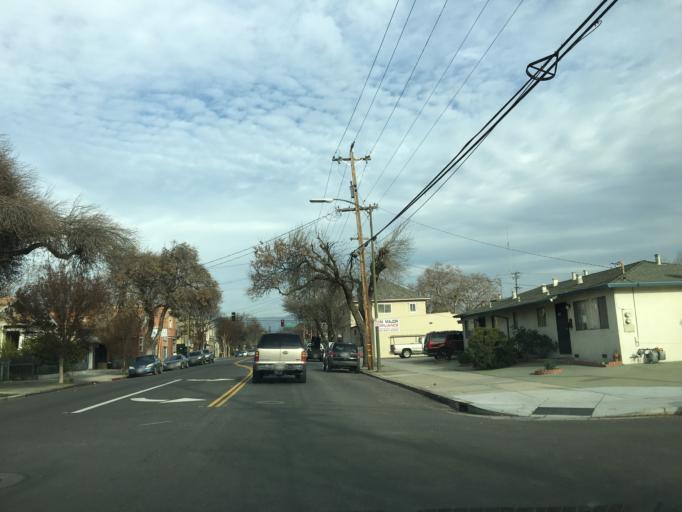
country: US
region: California
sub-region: Santa Clara County
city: San Jose
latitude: 37.3545
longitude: -121.8888
